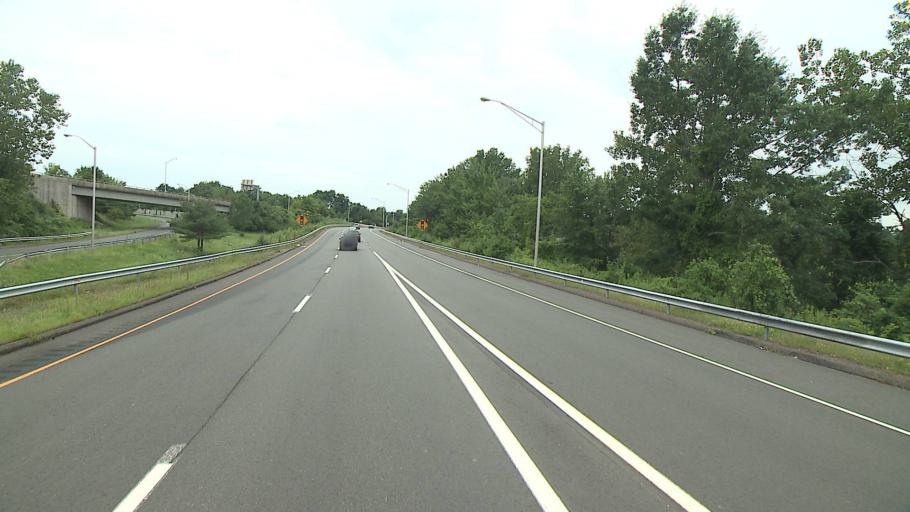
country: US
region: Connecticut
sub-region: Hartford County
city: Wethersfield
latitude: 41.7063
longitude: -72.6476
